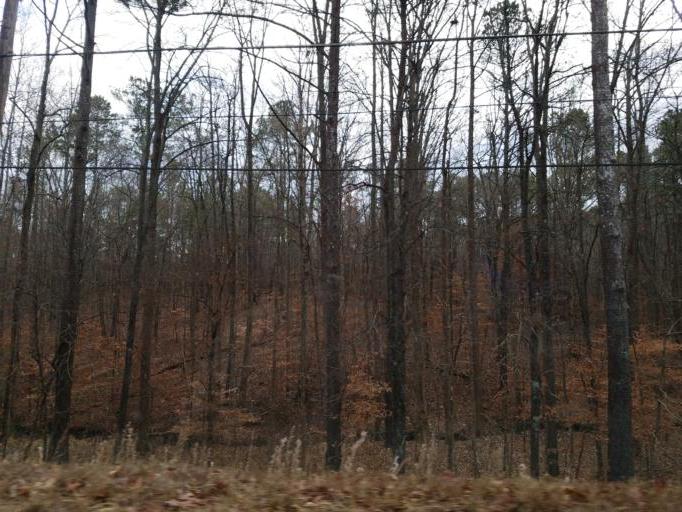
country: US
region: Georgia
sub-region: Cherokee County
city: Holly Springs
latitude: 34.2125
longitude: -84.5552
